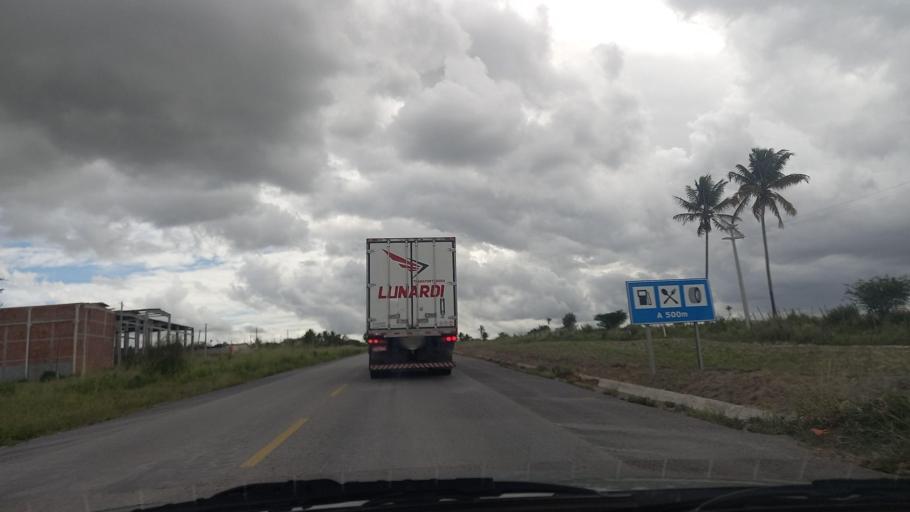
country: BR
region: Pernambuco
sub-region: Lajedo
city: Lajedo
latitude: -8.6652
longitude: -36.3609
